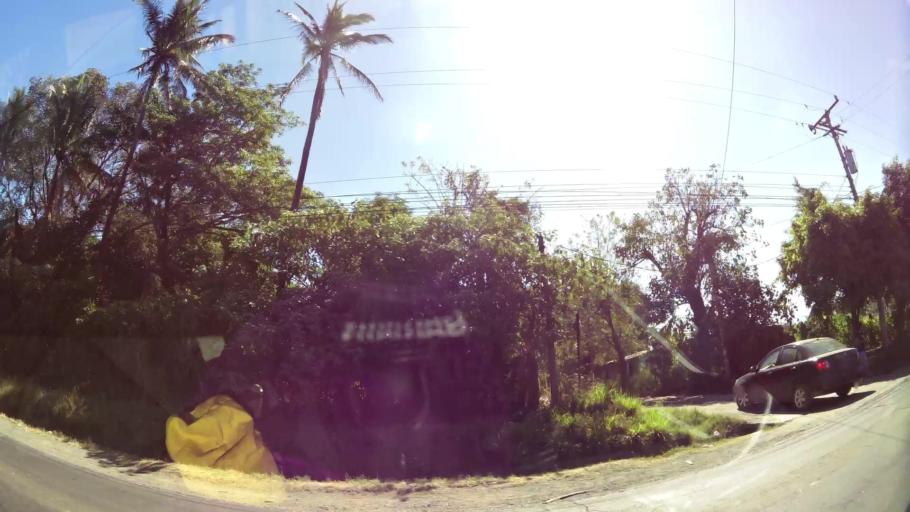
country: SV
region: La Libertad
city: San Juan Opico
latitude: 13.7854
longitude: -89.3713
